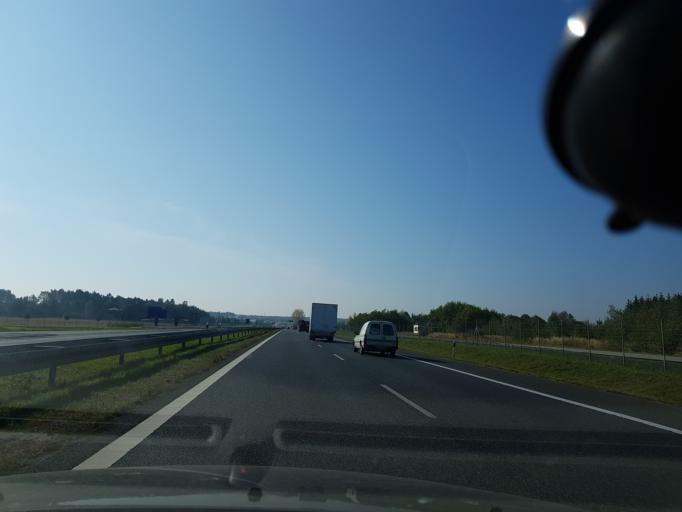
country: PL
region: Masovian Voivodeship
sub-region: Powiat zyrardowski
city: Mszczonow
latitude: 51.9502
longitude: 20.4899
